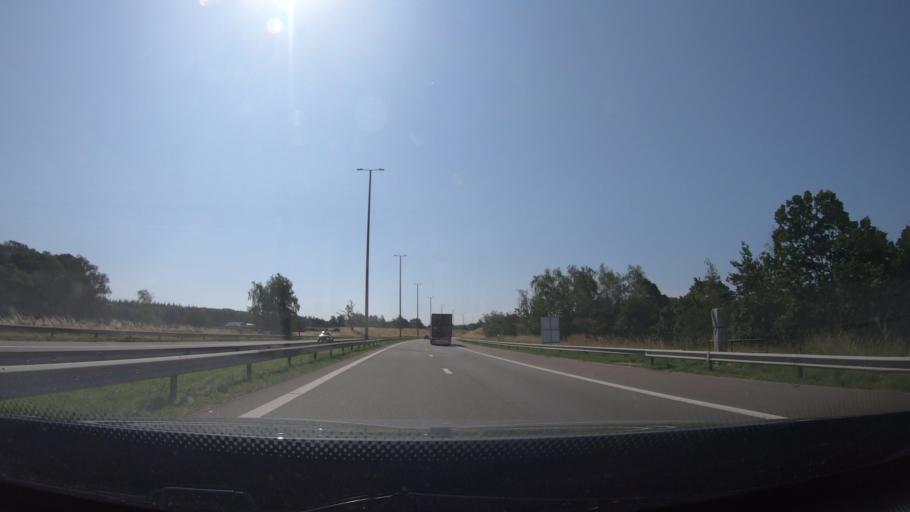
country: BE
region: Wallonia
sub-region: Province de Liege
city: Jalhay
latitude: 50.5212
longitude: 5.9403
